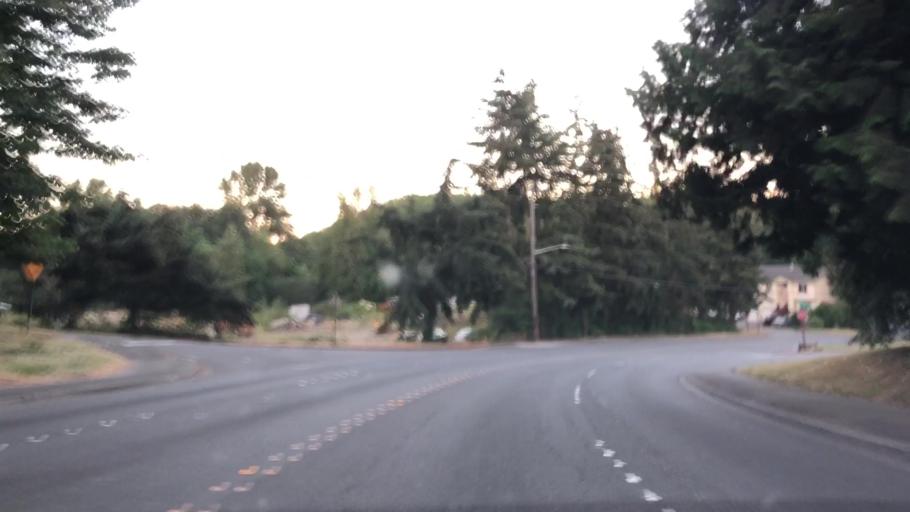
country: US
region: Washington
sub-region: King County
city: Riverton
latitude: 47.5075
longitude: -122.2735
